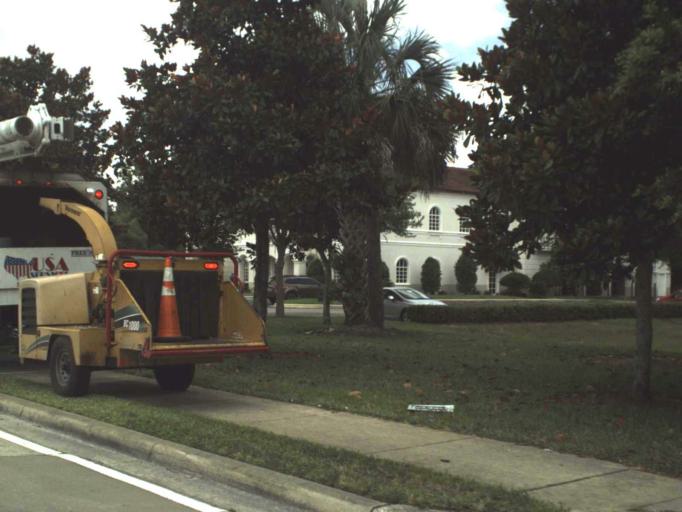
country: US
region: Florida
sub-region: Volusia County
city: DeLand
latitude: 29.0281
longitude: -81.2961
